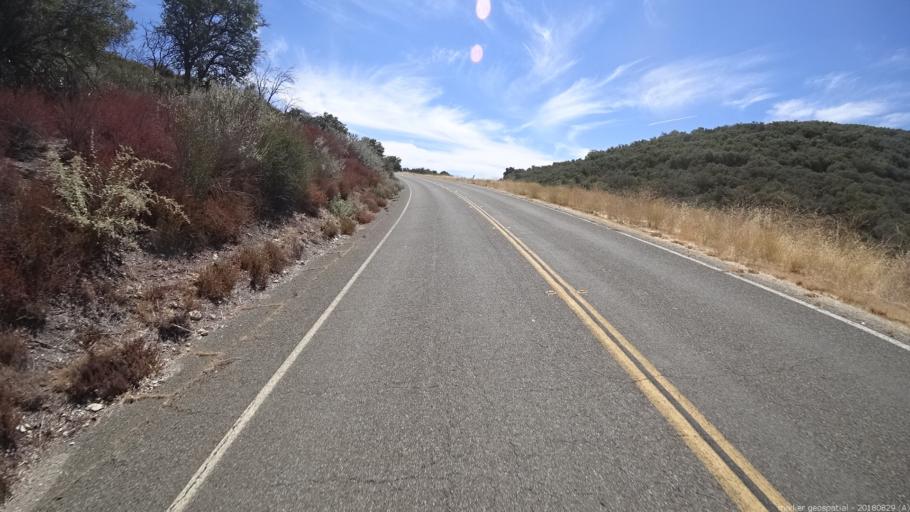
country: US
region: California
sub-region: San Luis Obispo County
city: Lake Nacimiento
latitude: 35.8517
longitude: -121.0539
